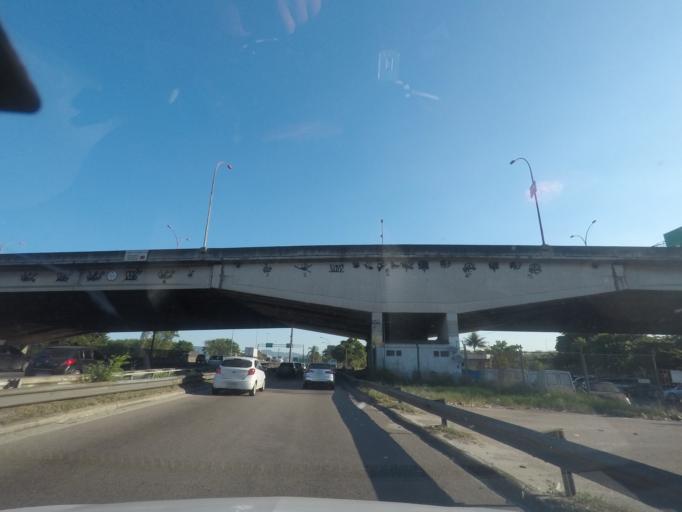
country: BR
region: Rio de Janeiro
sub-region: Duque De Caxias
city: Duque de Caxias
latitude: -22.8076
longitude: -43.2893
